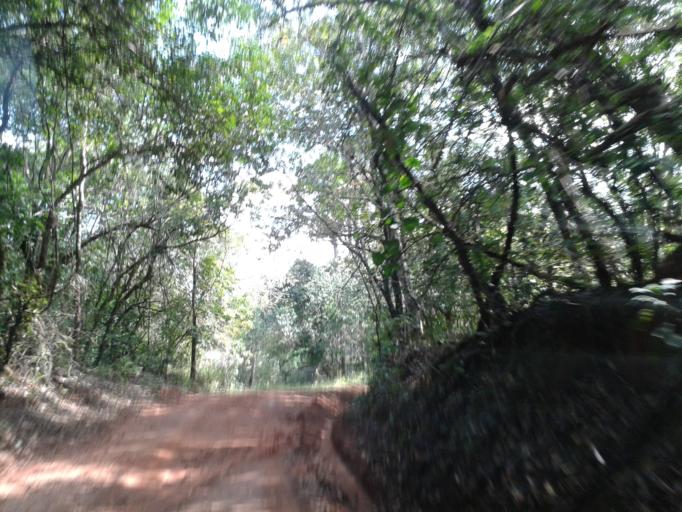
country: BR
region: Minas Gerais
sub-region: Campina Verde
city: Campina Verde
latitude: -19.3920
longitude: -49.6508
